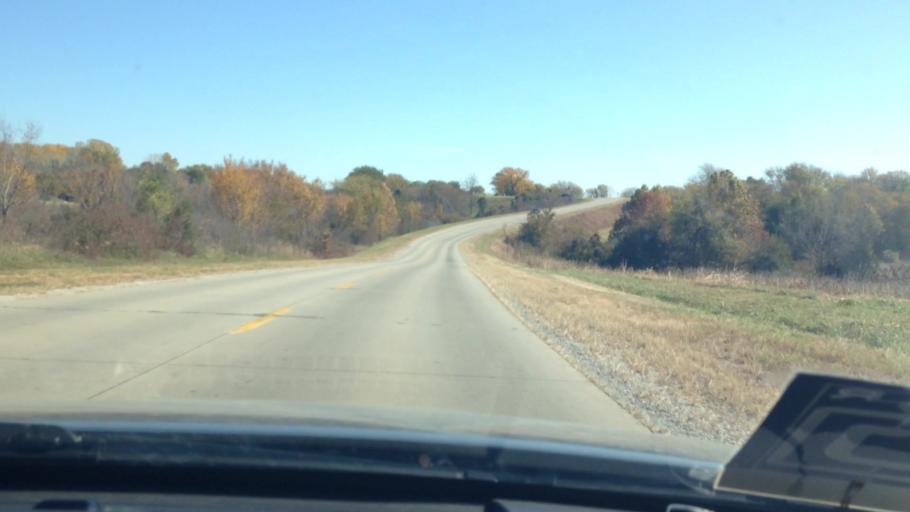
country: US
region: Missouri
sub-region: Platte County
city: Platte City
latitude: 39.3396
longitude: -94.7374
